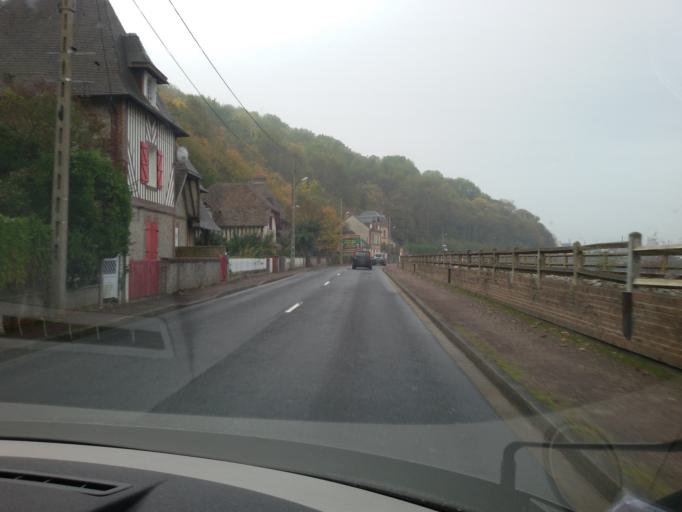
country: FR
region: Lower Normandy
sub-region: Departement du Calvados
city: Houlgate
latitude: 49.2966
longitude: -0.0871
